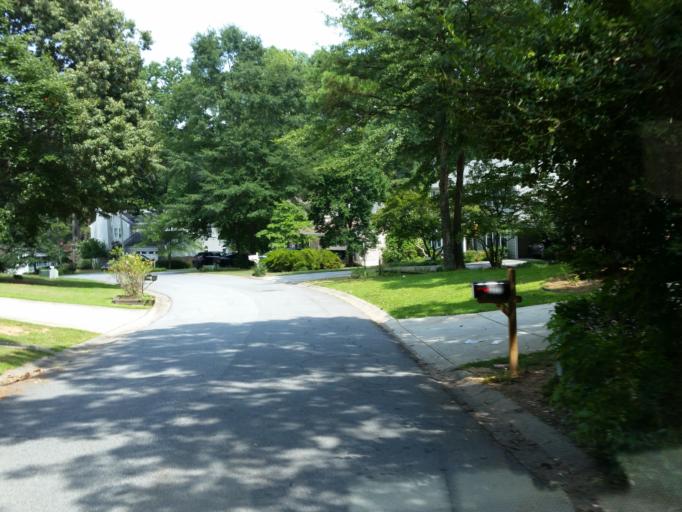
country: US
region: Georgia
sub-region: Cobb County
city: Marietta
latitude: 33.9656
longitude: -84.4777
